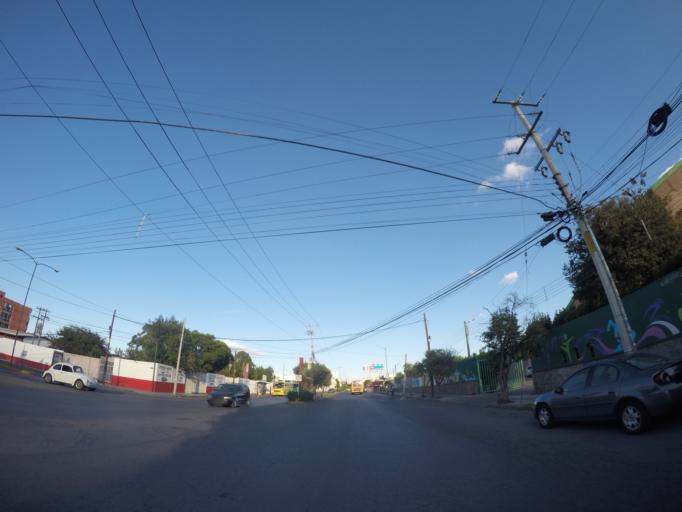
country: MX
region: San Luis Potosi
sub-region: San Luis Potosi
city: San Luis Potosi
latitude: 22.1375
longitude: -100.9859
